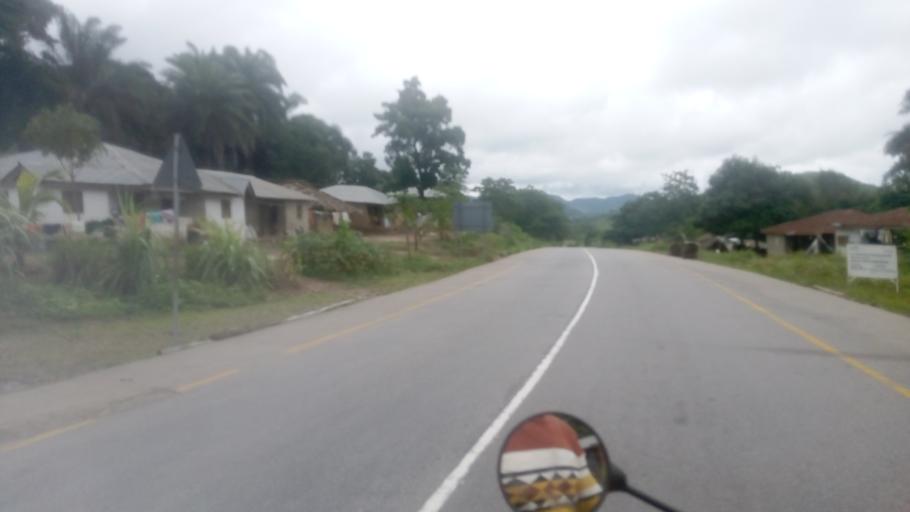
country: SL
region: Northern Province
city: Masaka
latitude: 8.6455
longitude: -11.7586
